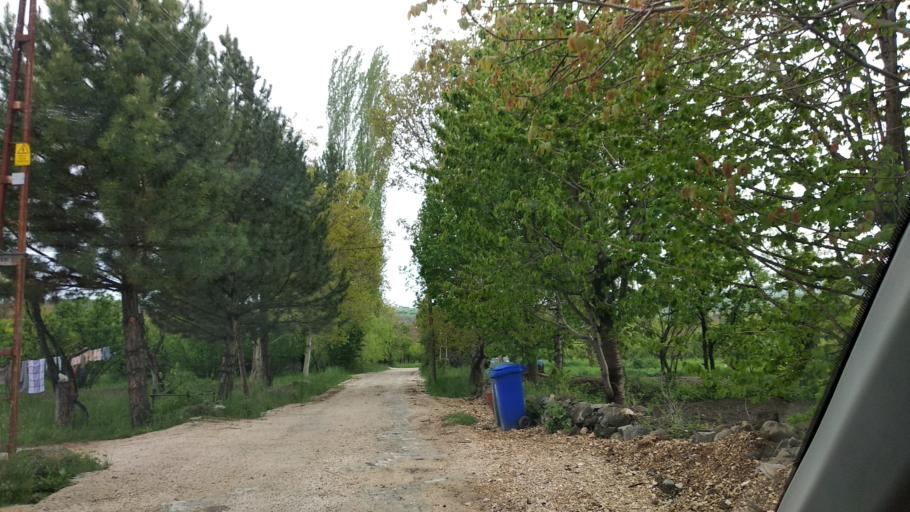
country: TR
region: Bolu
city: Seben
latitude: 40.4144
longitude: 31.5645
